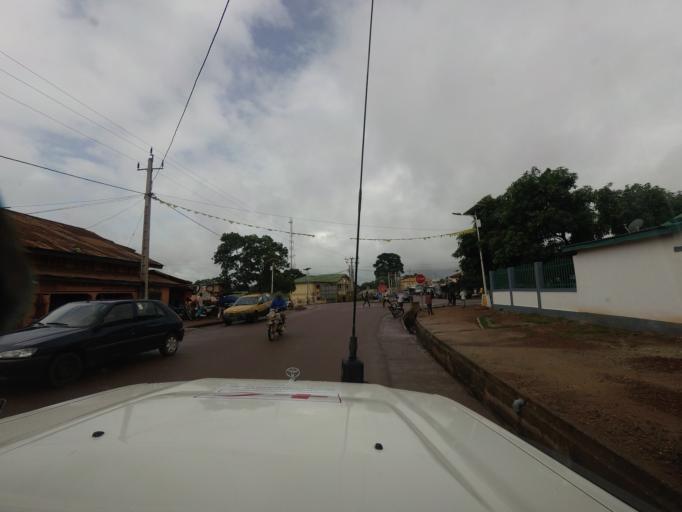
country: GN
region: Nzerekore
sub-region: Nzerekore Prefecture
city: Nzerekore
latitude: 7.7490
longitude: -8.8192
